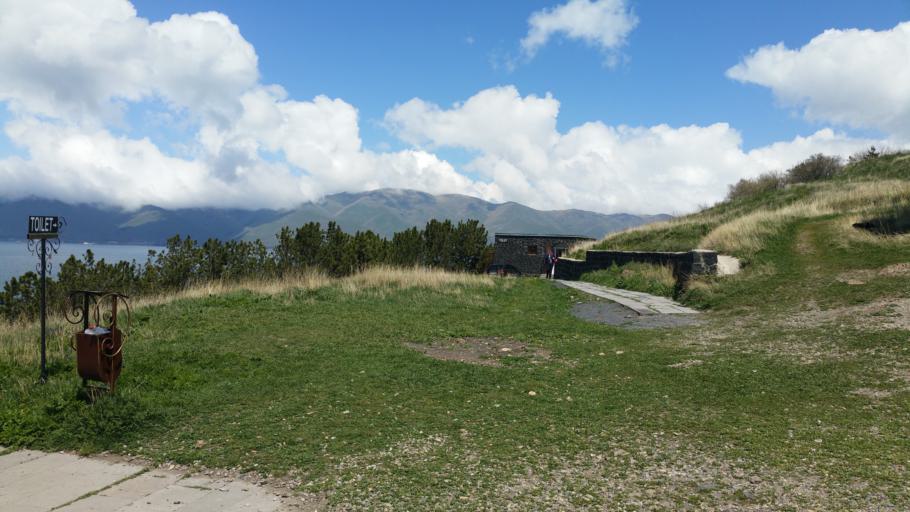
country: AM
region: Geghark'unik'i Marz
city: Sevan
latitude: 40.5640
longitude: 45.0094
